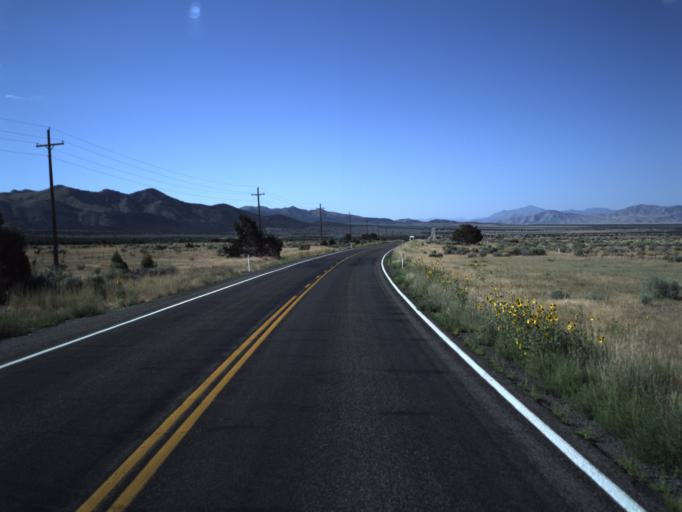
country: US
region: Utah
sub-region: Juab County
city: Mona
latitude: 39.9017
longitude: -112.1381
